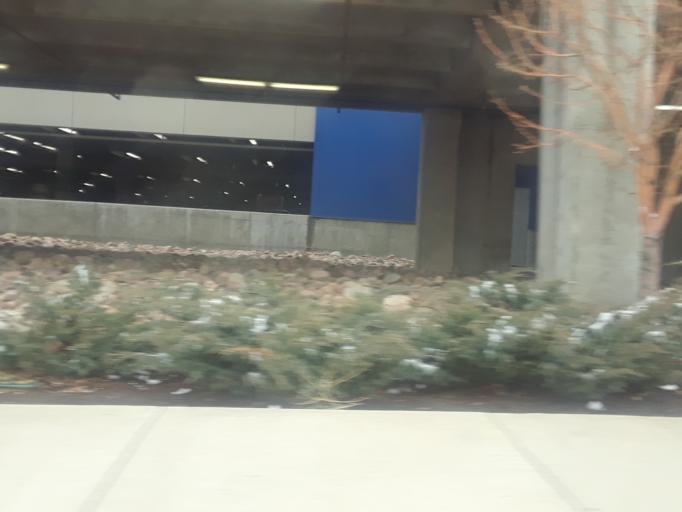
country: US
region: Colorado
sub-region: Arapahoe County
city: Centennial
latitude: 39.5708
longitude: -104.8750
